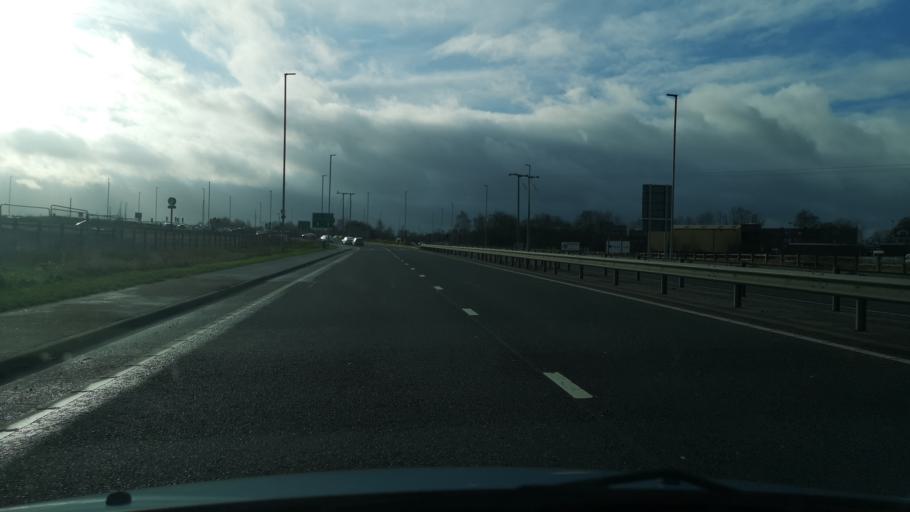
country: GB
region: England
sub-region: Barnsley
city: Birdwell
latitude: 53.5010
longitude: -1.4727
